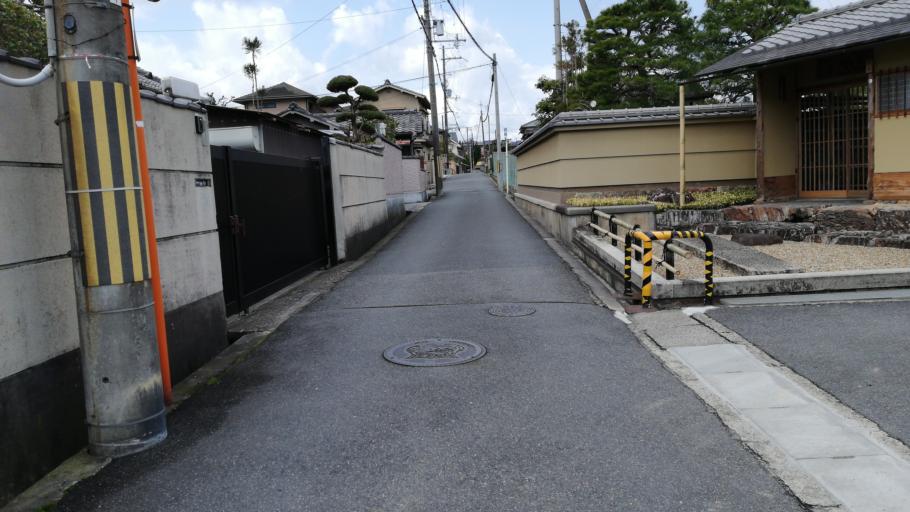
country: JP
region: Nara
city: Nara-shi
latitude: 34.6476
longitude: 135.7785
